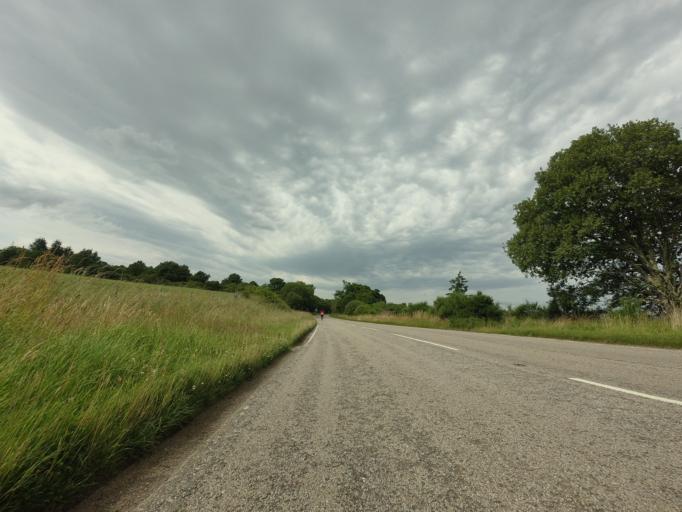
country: GB
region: Scotland
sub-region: Highland
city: Alness
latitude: 57.8745
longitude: -4.3548
